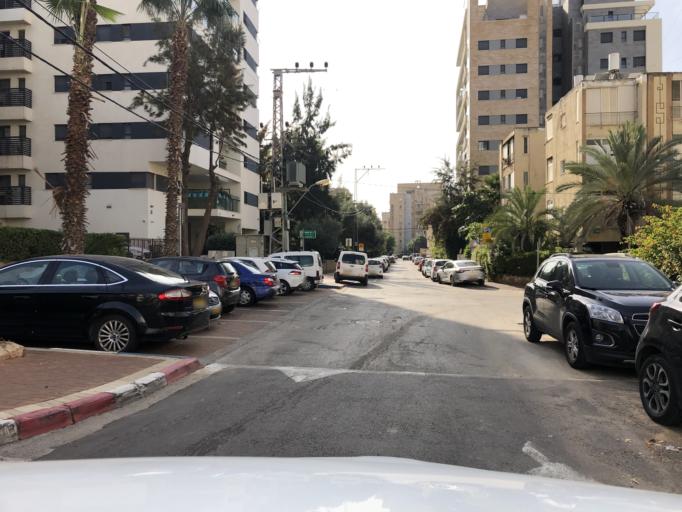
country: IL
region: Tel Aviv
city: Bene Beraq
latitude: 32.0693
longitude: 34.8308
